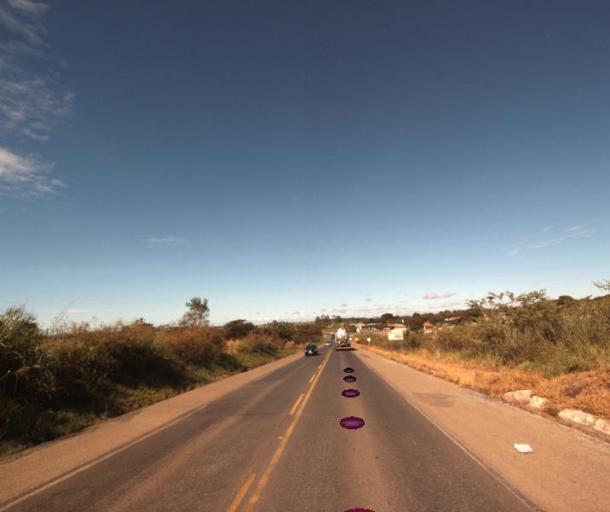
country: BR
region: Goias
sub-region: Itapaci
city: Itapaci
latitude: -14.8608
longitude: -49.3246
